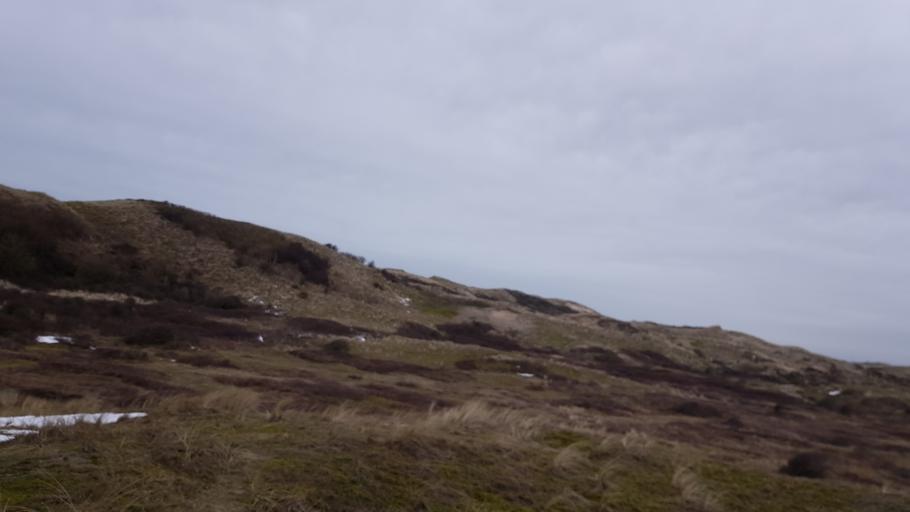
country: NL
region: North Holland
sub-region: Gemeente Bergen
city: Egmond aan Zee
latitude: 52.5930
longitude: 4.6185
